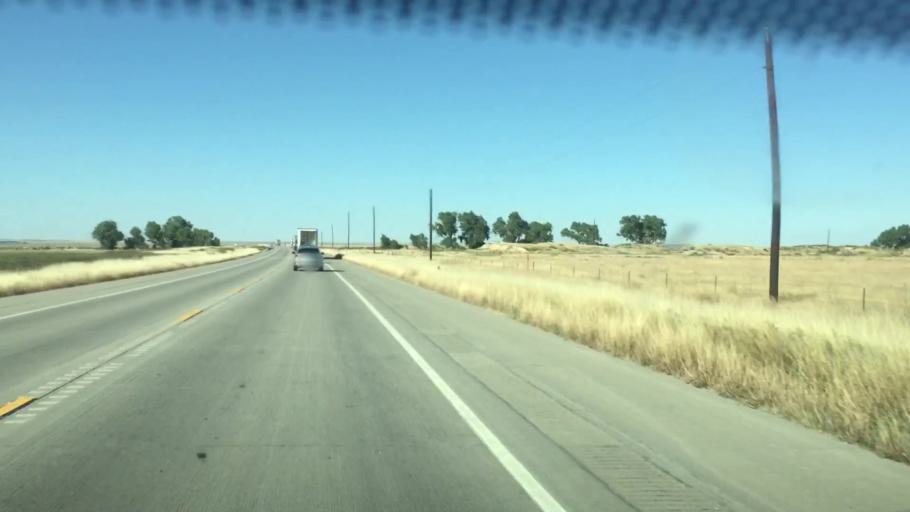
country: US
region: Colorado
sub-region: Kiowa County
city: Eads
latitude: 38.3302
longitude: -102.7198
